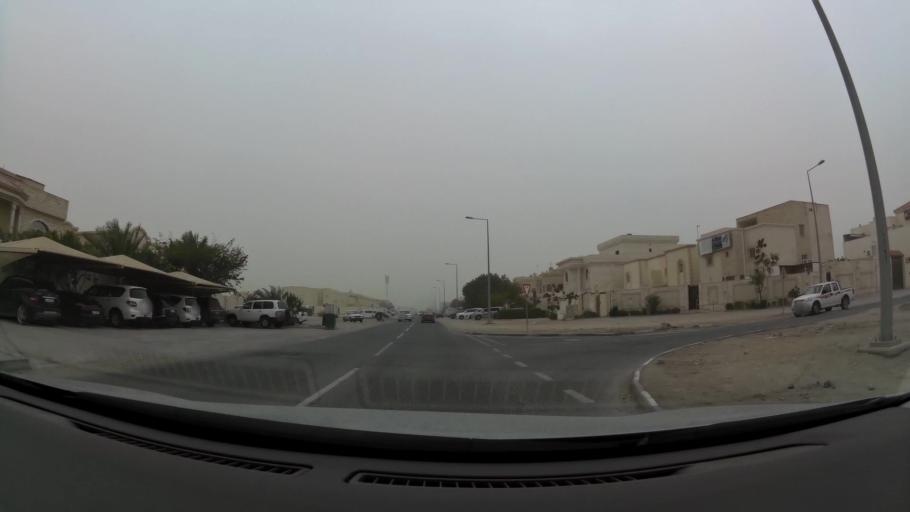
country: QA
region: Baladiyat ad Dawhah
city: Doha
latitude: 25.2425
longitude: 51.4888
